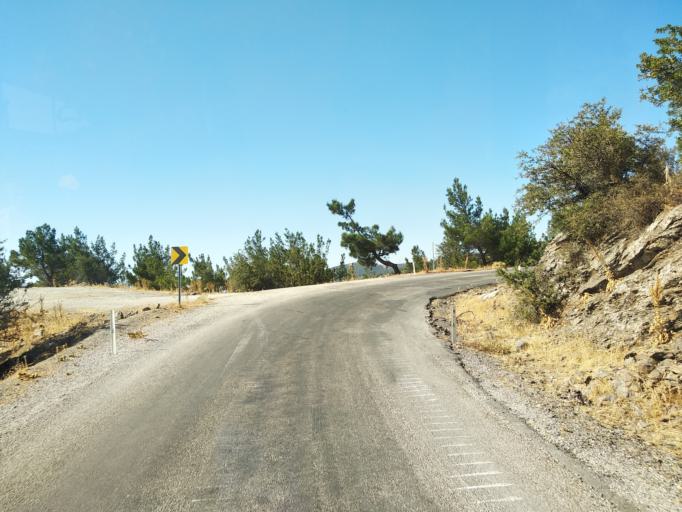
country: TR
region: Izmir
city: Gaziemir
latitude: 38.2995
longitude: 26.9956
